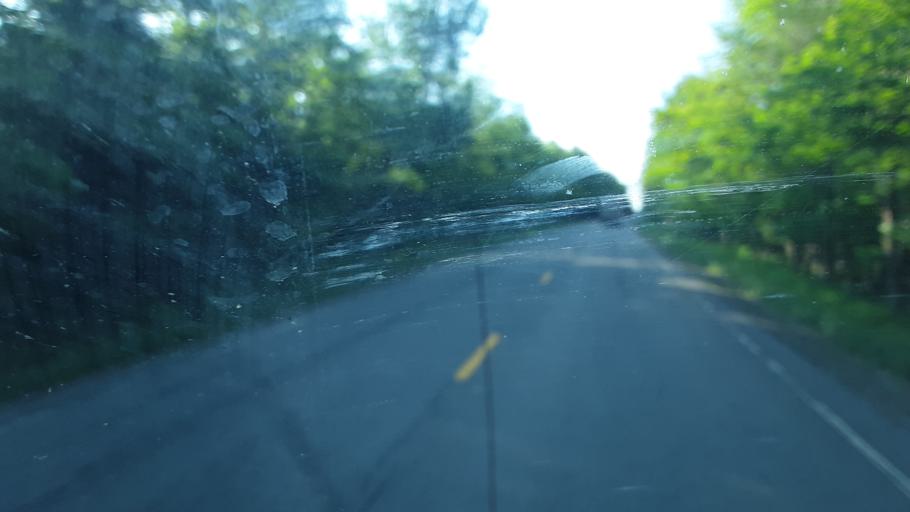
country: US
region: Maine
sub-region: Penobscot County
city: Patten
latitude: 46.1951
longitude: -68.2628
